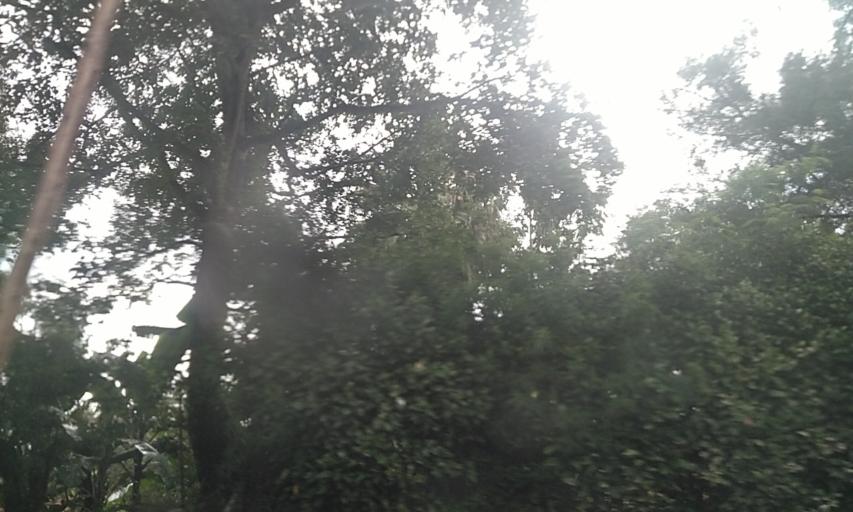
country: UG
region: Central Region
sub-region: Kampala District
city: Kampala
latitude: 0.3304
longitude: 32.5966
